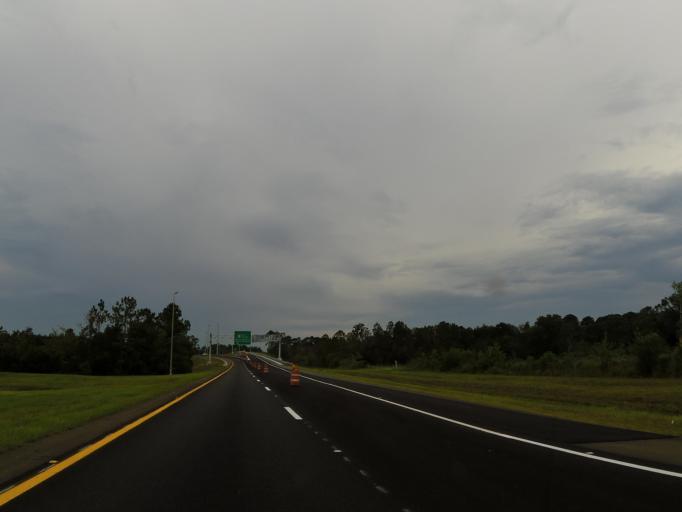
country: US
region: Florida
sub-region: Duval County
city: Baldwin
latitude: 30.3087
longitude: -81.8722
